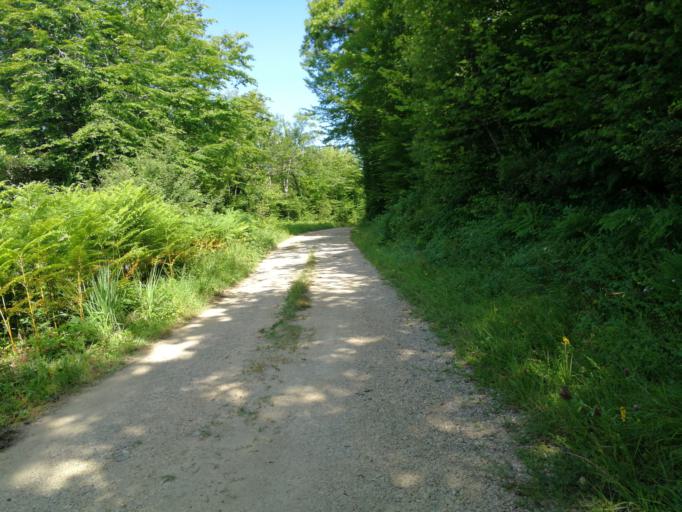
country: FR
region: Franche-Comte
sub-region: Departement du Jura
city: Moirans-en-Montagne
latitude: 46.4489
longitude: 5.6685
